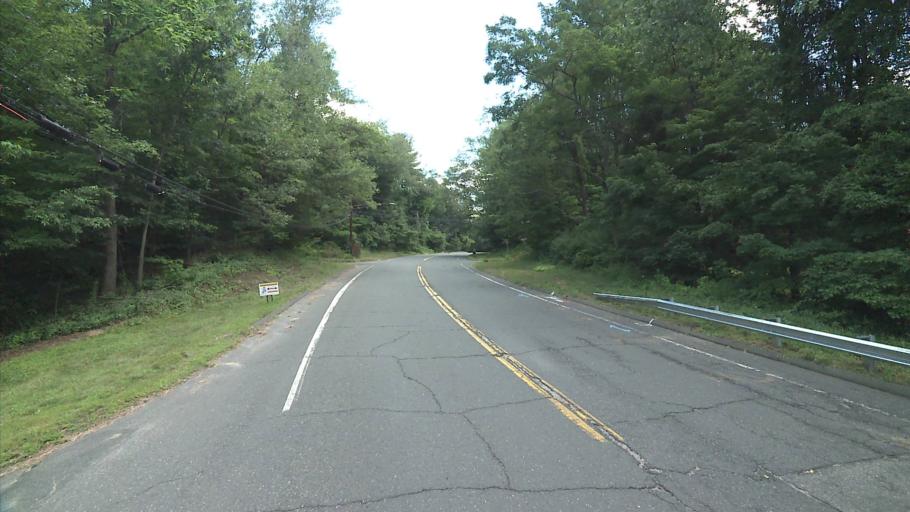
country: US
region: Connecticut
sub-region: Litchfield County
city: New Hartford Center
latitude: 41.8807
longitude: -72.9682
